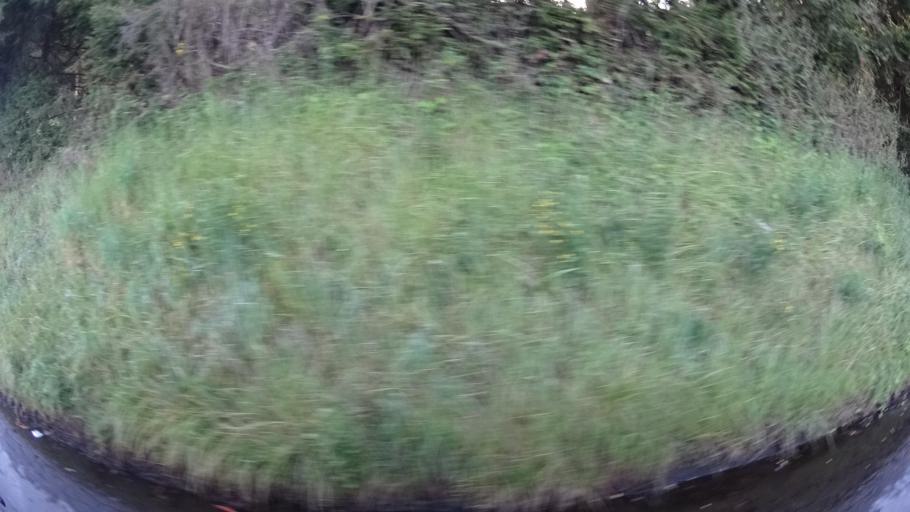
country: US
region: California
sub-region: Humboldt County
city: Myrtletown
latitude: 40.7780
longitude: -124.1185
